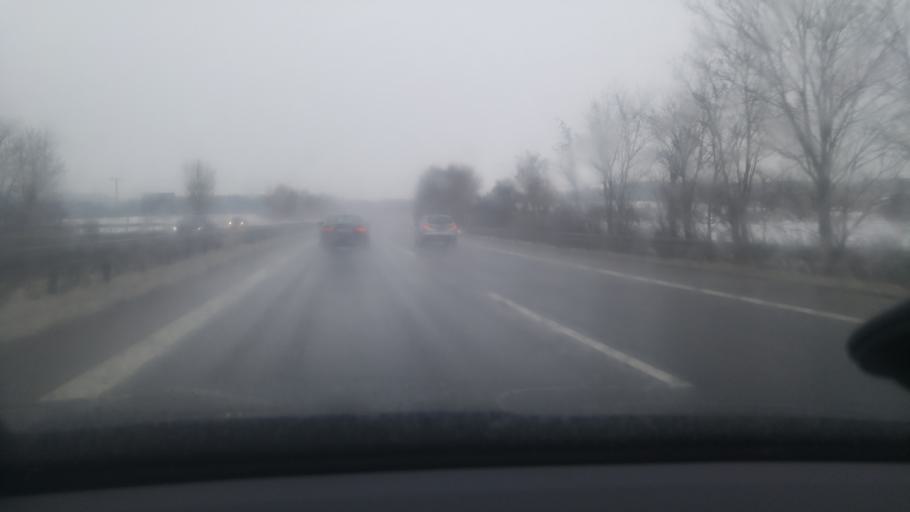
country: DE
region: Baden-Wuerttemberg
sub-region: Freiburg Region
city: Dietingen
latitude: 48.2336
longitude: 8.6505
